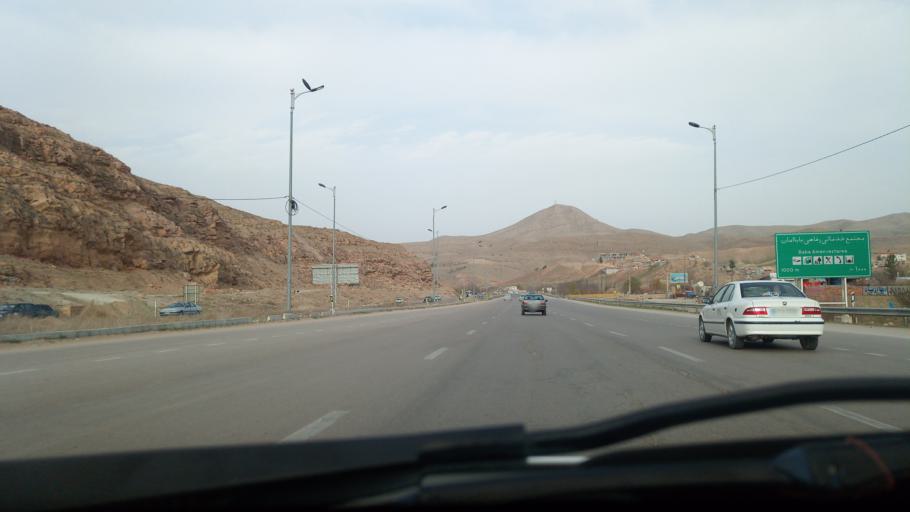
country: IR
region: Khorasan-e Shomali
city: Bojnurd
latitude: 37.4772
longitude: 57.4286
